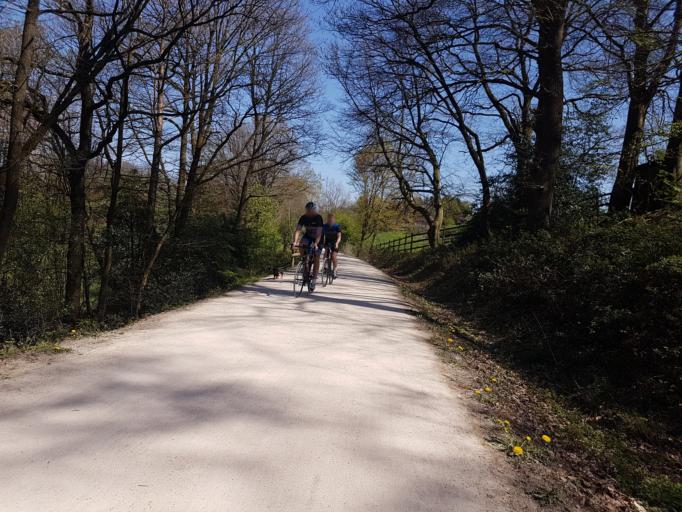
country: DE
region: North Rhine-Westphalia
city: Sprockhovel
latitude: 51.3375
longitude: 7.2845
